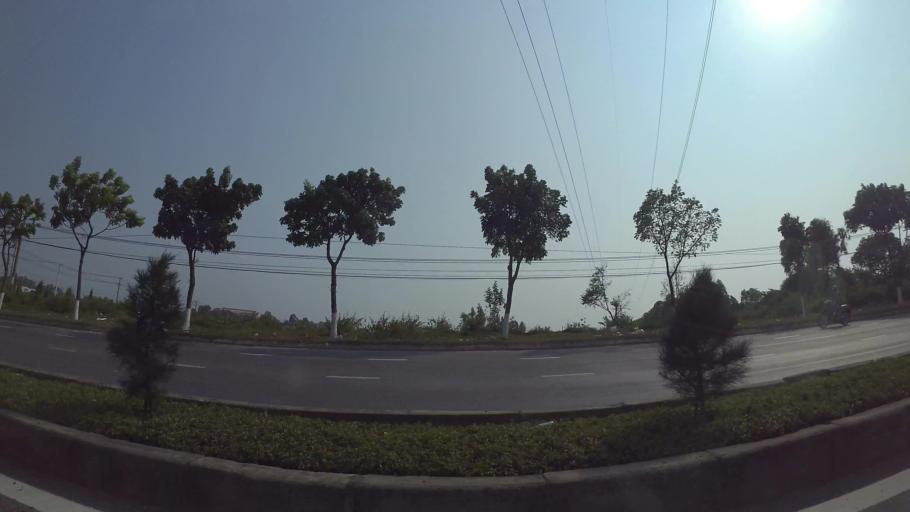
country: VN
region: Da Nang
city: Cam Le
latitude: 16.0116
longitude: 108.1846
